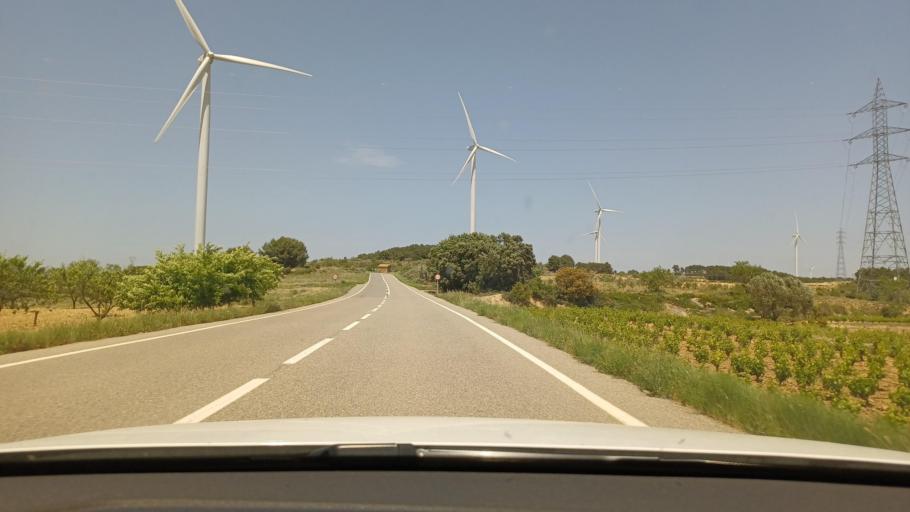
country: ES
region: Catalonia
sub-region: Provincia de Tarragona
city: Vilalba dels Arcs
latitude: 41.0983
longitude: 0.4176
